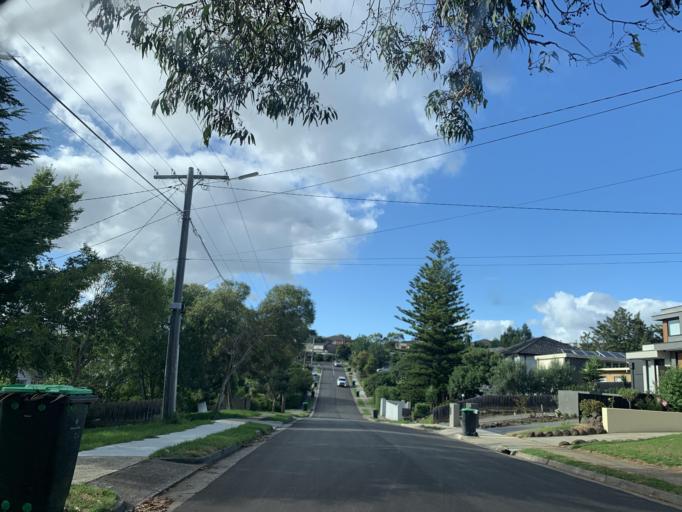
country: AU
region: Victoria
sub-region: Moreland
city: Oak Park
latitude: -37.7207
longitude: 144.9075
